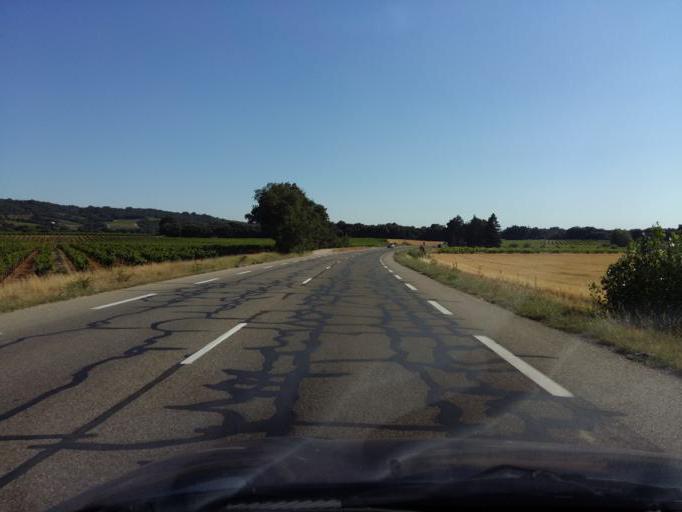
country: FR
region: Provence-Alpes-Cote d'Azur
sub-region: Departement du Vaucluse
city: Visan
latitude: 44.3462
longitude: 4.9544
